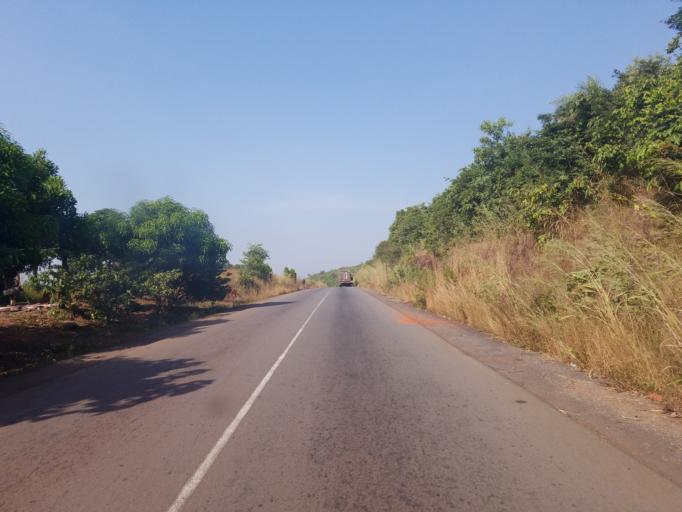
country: GN
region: Boke
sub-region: Boffa
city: Boffa
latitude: 10.1391
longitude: -13.9848
